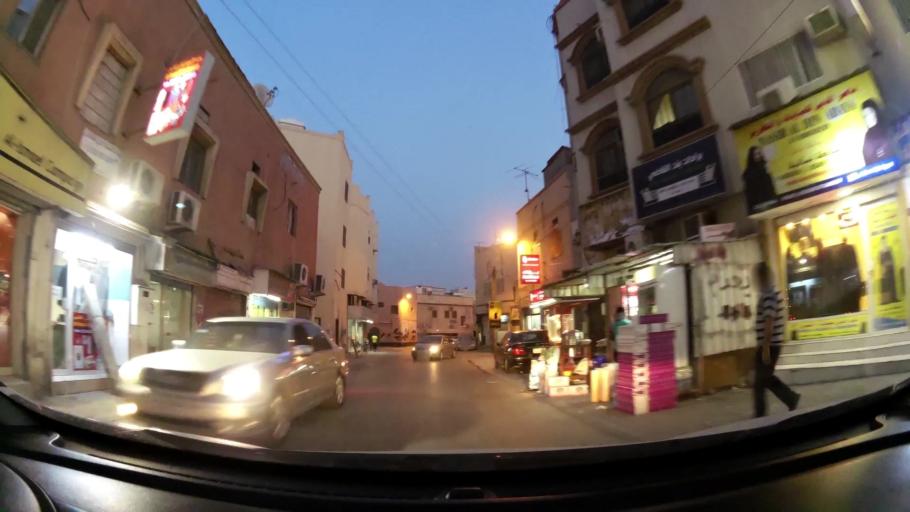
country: BH
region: Manama
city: Jidd Hafs
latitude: 26.2057
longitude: 50.5506
